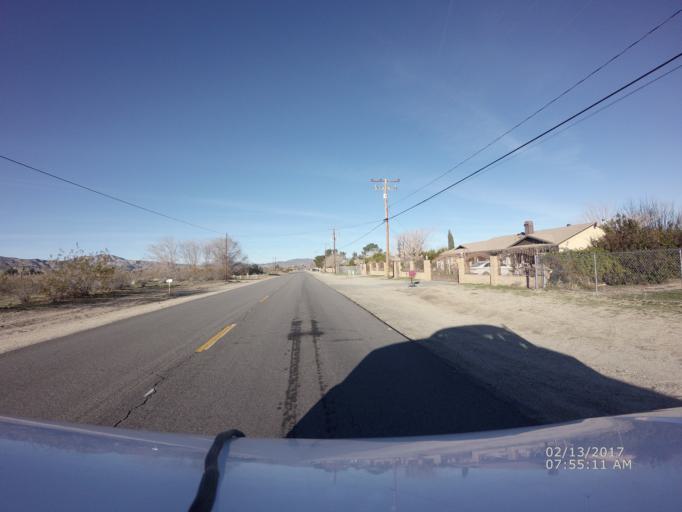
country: US
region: California
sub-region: Los Angeles County
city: Littlerock
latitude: 34.5287
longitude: -117.9683
